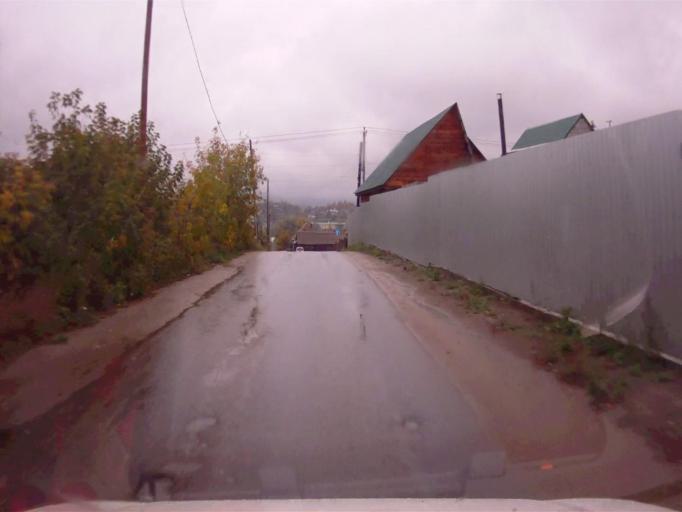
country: RU
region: Chelyabinsk
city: Kyshtym
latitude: 55.7144
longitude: 60.5536
